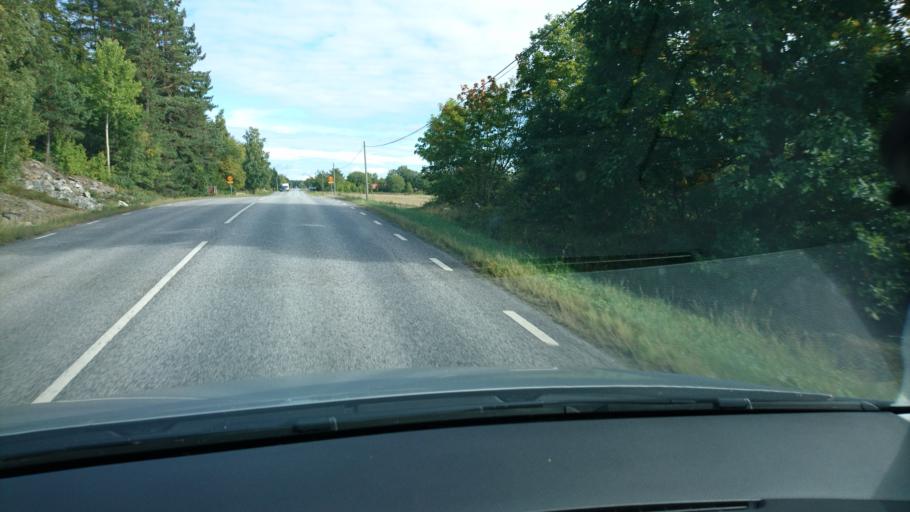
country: SE
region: Soedermanland
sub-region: Strangnas Kommun
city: Stallarholmen
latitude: 59.3523
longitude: 17.1938
